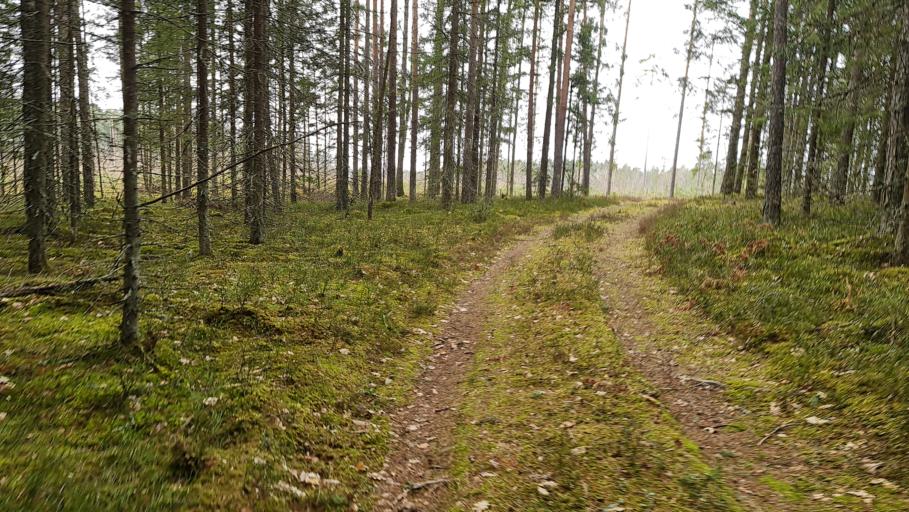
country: BY
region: Vitebsk
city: Byahoml'
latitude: 54.7128
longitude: 27.9459
